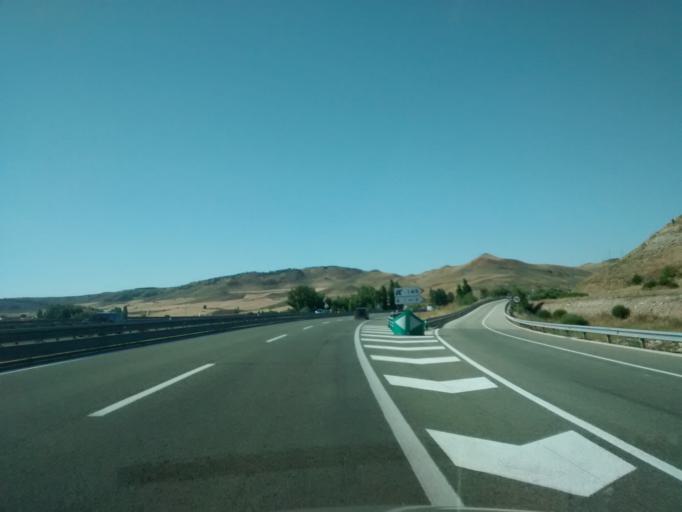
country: ES
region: Castille and Leon
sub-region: Provincia de Soria
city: Medinaceli
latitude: 41.1256
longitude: -2.4468
